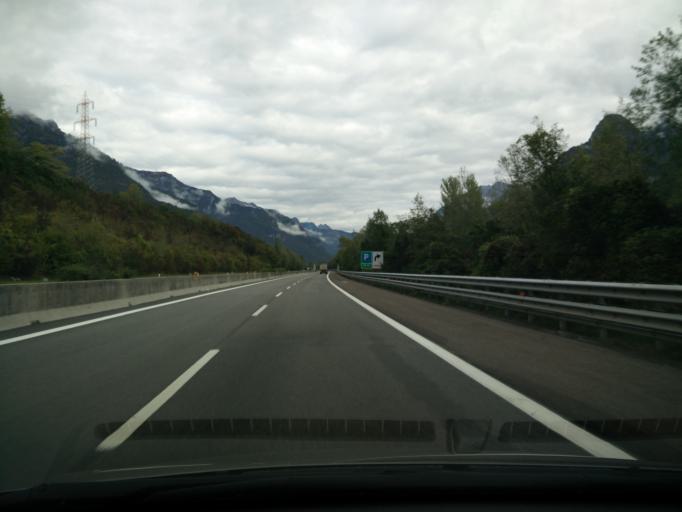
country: IT
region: Veneto
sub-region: Provincia di Belluno
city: Ponte nelle Alpi-Polpet
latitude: 46.1912
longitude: 12.2897
